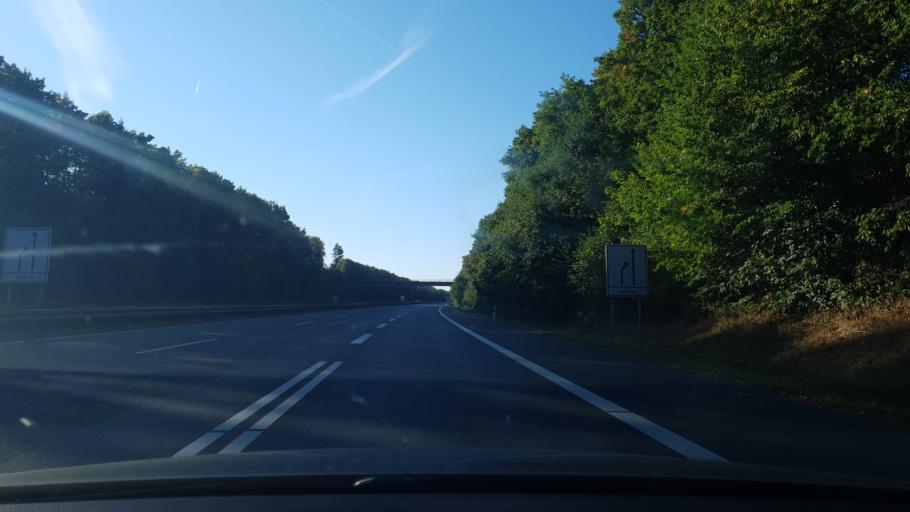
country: DE
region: Hesse
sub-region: Regierungsbezirk Giessen
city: Langgons
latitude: 50.4907
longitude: 8.6549
